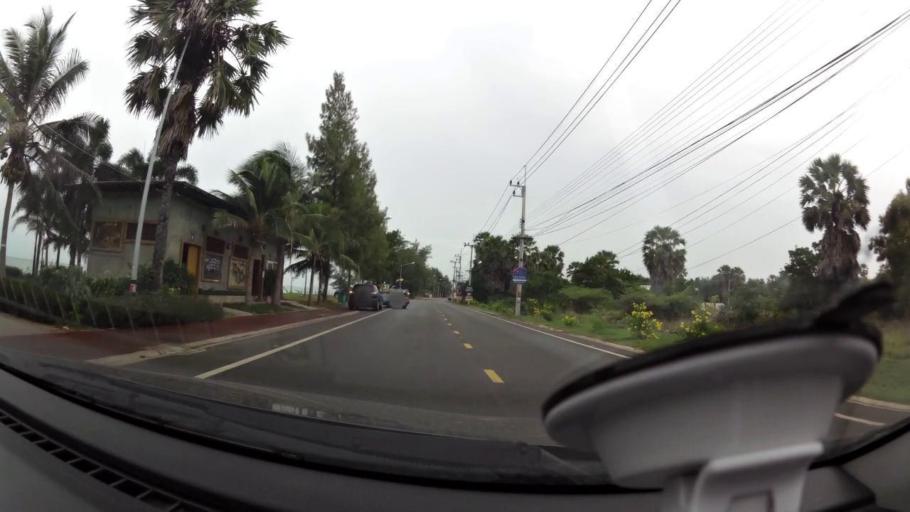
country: TH
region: Prachuap Khiri Khan
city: Pran Buri
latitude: 12.3705
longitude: 100.0000
